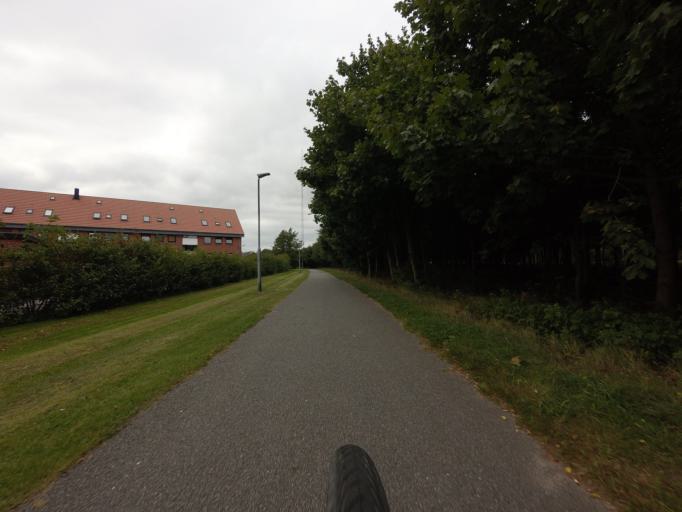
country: DK
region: South Denmark
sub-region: Billund Kommune
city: Grindsted
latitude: 55.7646
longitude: 8.9240
